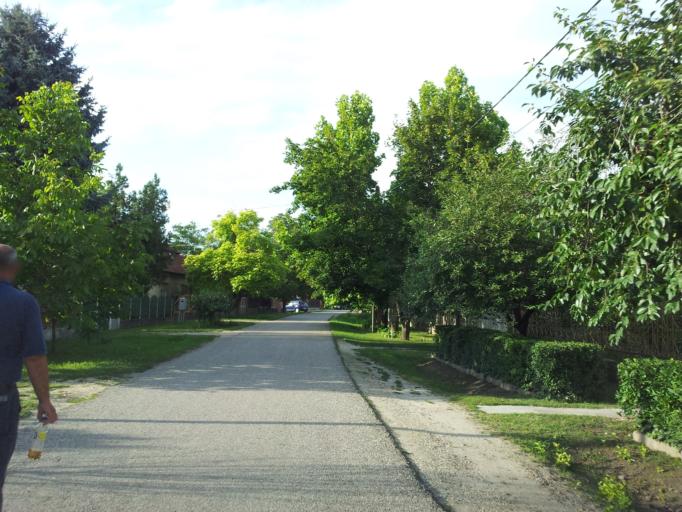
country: HU
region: Pest
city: Kiskunlachaza
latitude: 47.1817
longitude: 19.0087
